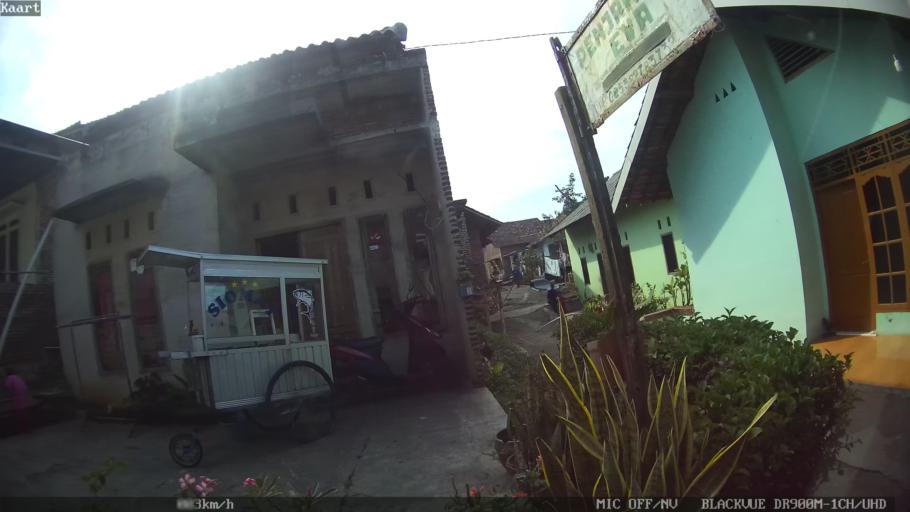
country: ID
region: Lampung
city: Kedaton
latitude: -5.3902
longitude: 105.2230
